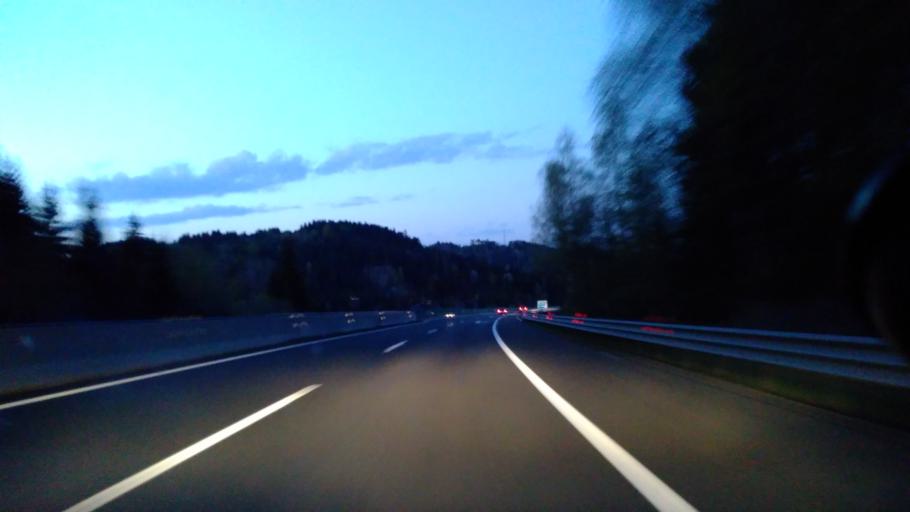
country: AT
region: Carinthia
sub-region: Politischer Bezirk Wolfsberg
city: Sankt Andrae
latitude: 46.7389
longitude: 14.8044
